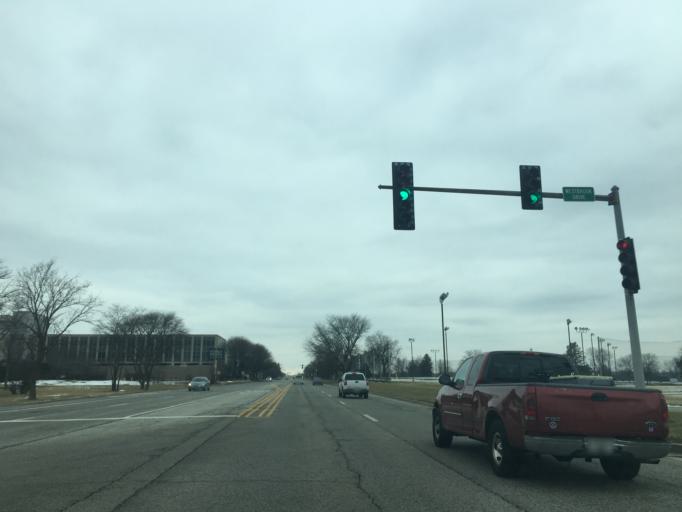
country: US
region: Illinois
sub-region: Cook County
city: Westchester
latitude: 41.8481
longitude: -87.9065
